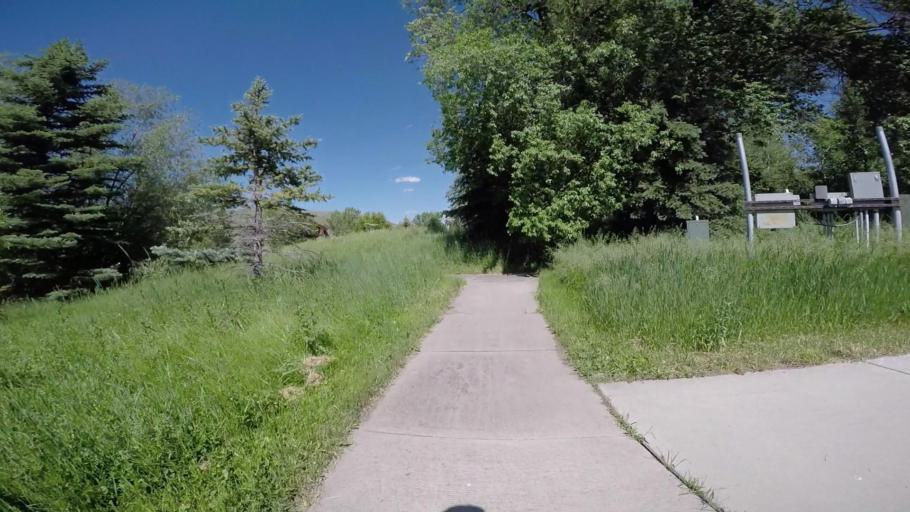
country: US
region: Utah
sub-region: Summit County
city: Park City
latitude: 40.6611
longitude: -111.5103
